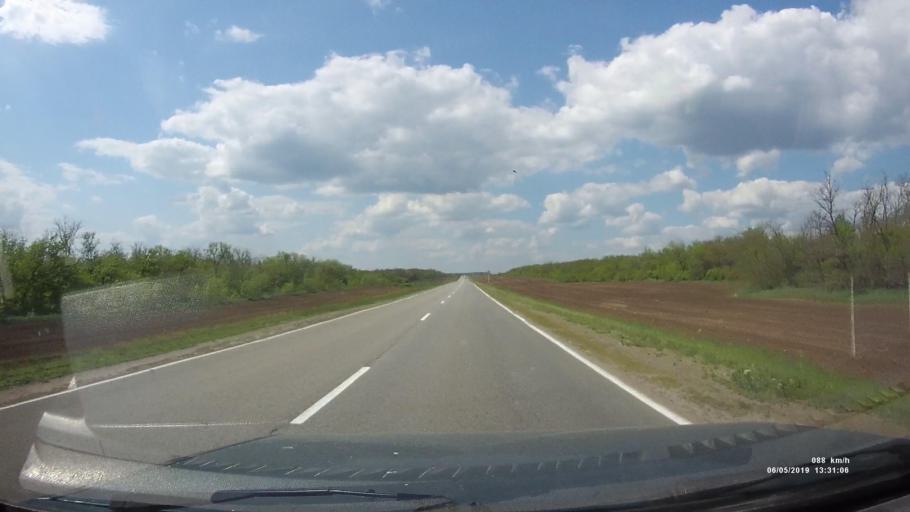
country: RU
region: Rostov
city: Ust'-Donetskiy
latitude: 47.6740
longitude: 40.8161
